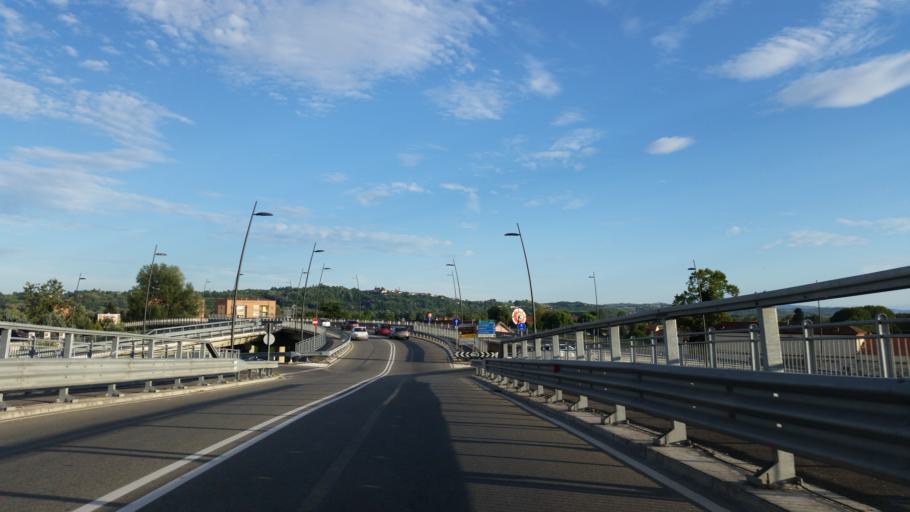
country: IT
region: Piedmont
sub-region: Provincia di Asti
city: Asti
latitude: 44.8930
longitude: 8.2004
